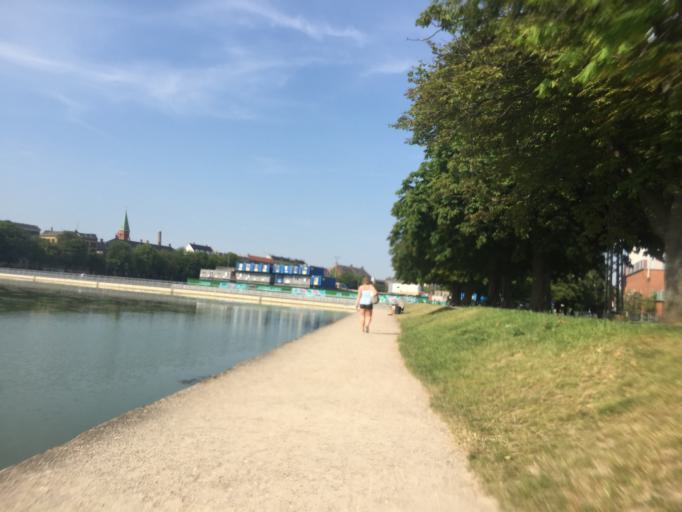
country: DK
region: Capital Region
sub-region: Kobenhavn
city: Copenhagen
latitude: 55.6937
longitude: 12.5755
